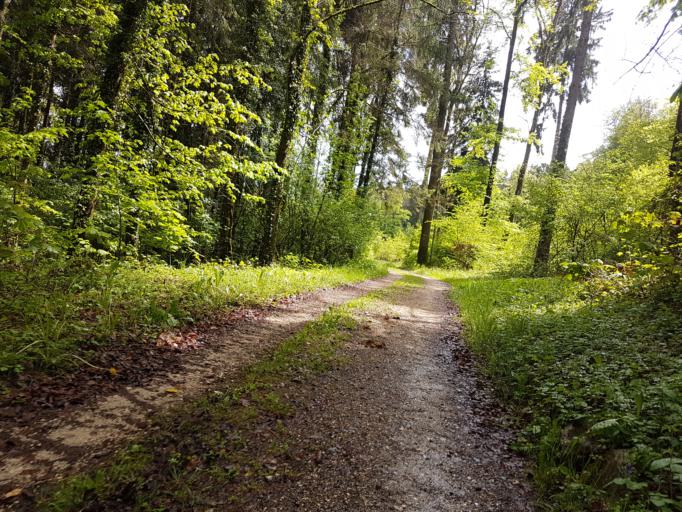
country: CH
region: Vaud
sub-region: Ouest Lausannois District
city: Bussigny
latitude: 46.5578
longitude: 6.5265
